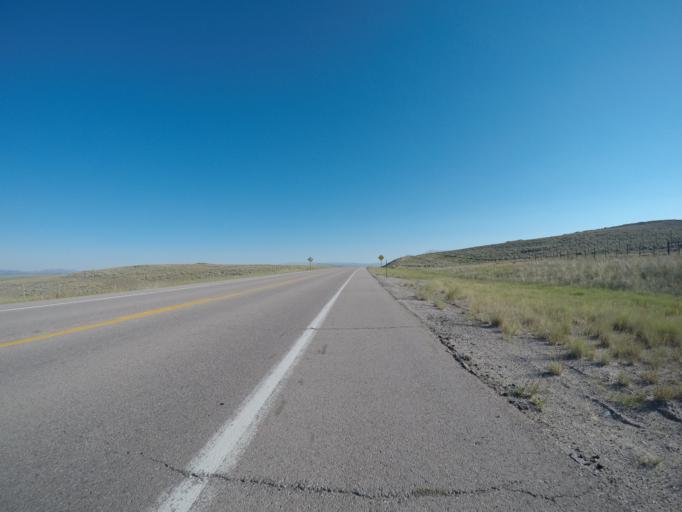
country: US
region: Wyoming
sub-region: Sublette County
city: Pinedale
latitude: 42.9194
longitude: -110.0800
